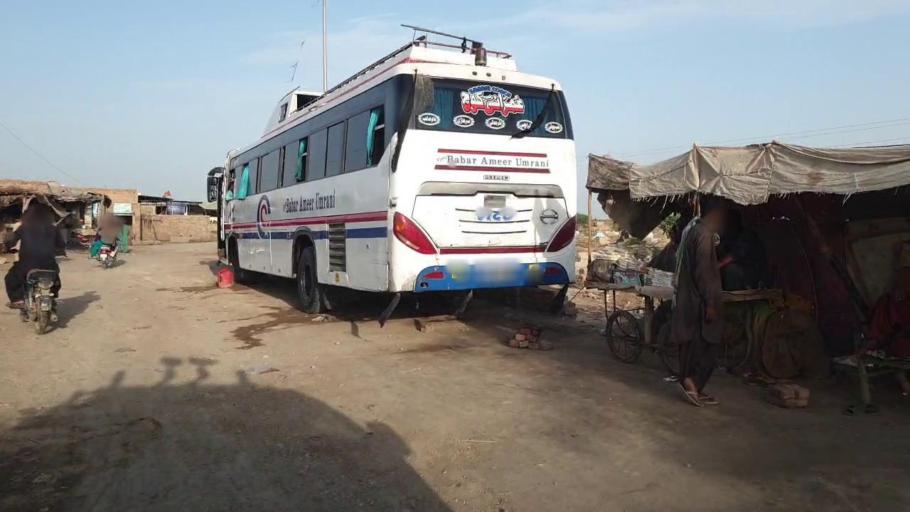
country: PK
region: Sindh
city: Jam Sahib
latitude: 26.2984
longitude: 68.6334
